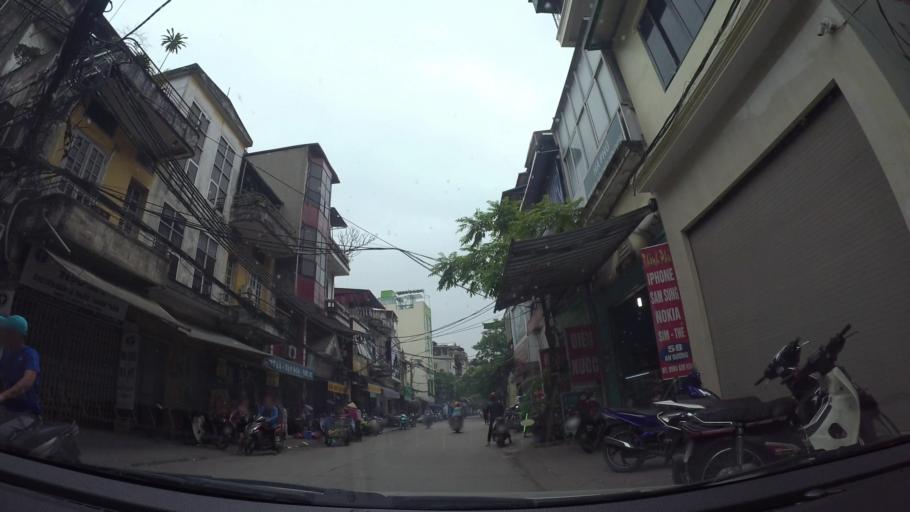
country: VN
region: Ha Noi
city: Hoan Kiem
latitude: 21.0529
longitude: 105.8405
